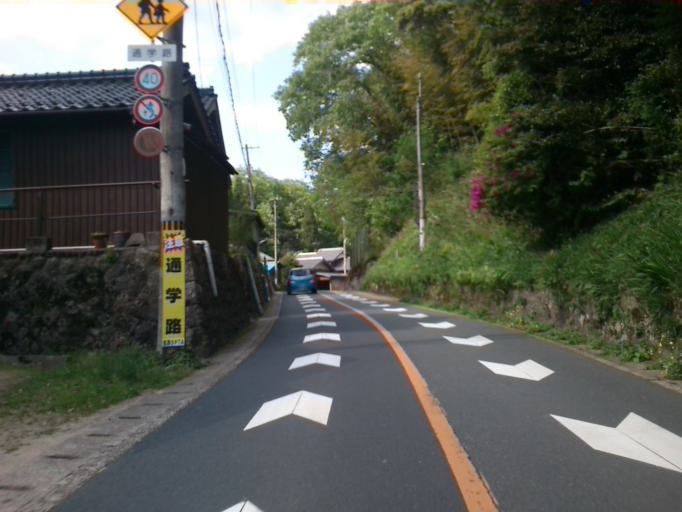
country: JP
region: Kyoto
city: Miyazu
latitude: 35.6824
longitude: 135.0568
